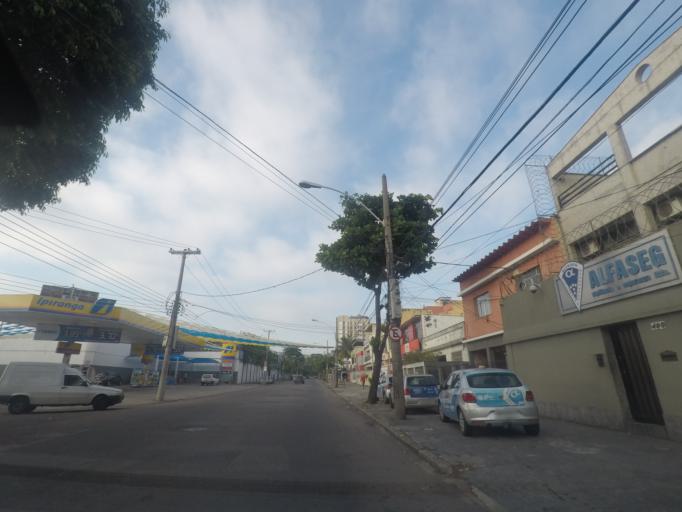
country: BR
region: Rio de Janeiro
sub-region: Duque De Caxias
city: Duque de Caxias
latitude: -22.8402
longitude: -43.2668
